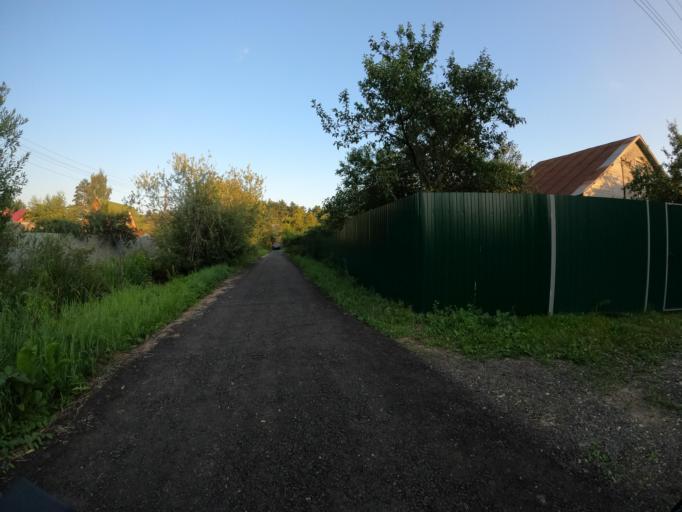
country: RU
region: Moskovskaya
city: Malyshevo
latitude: 55.5207
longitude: 38.3224
